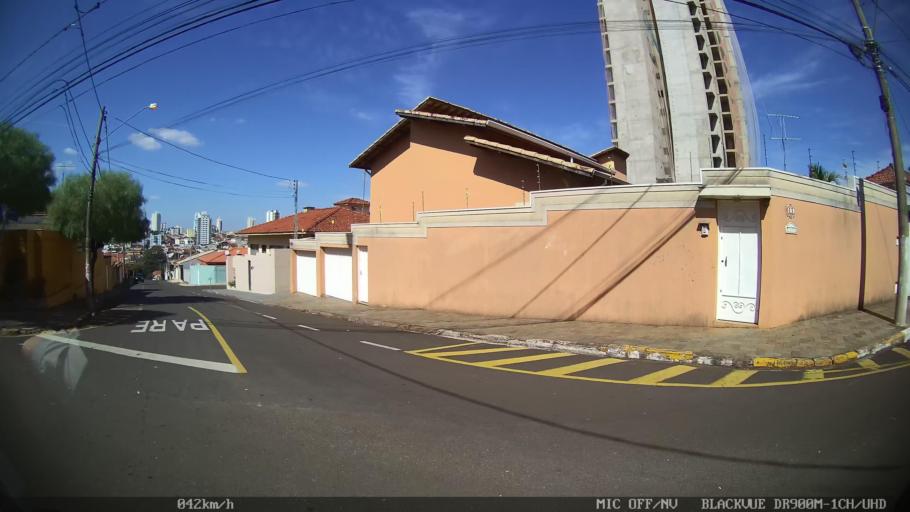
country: BR
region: Sao Paulo
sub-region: Franca
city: Franca
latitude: -20.5363
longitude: -47.4108
